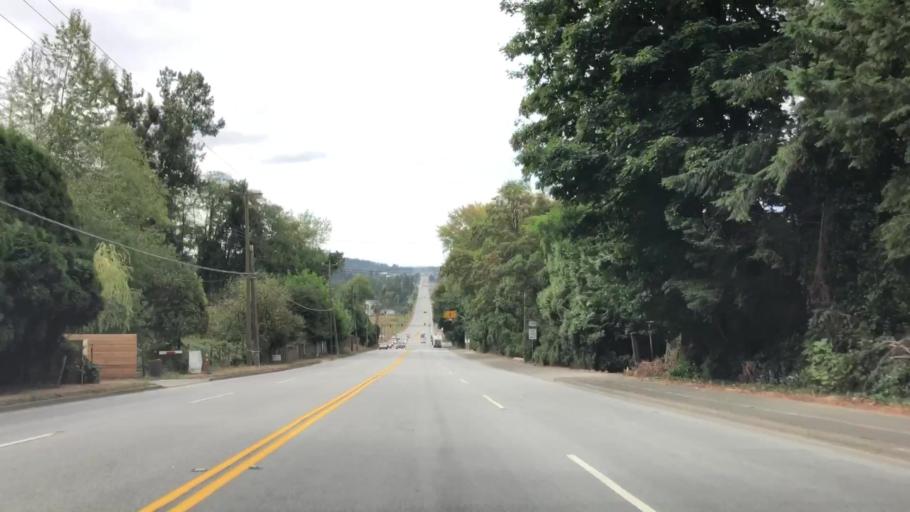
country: US
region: Washington
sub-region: Whatcom County
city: Blaine
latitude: 49.0339
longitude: -122.7352
